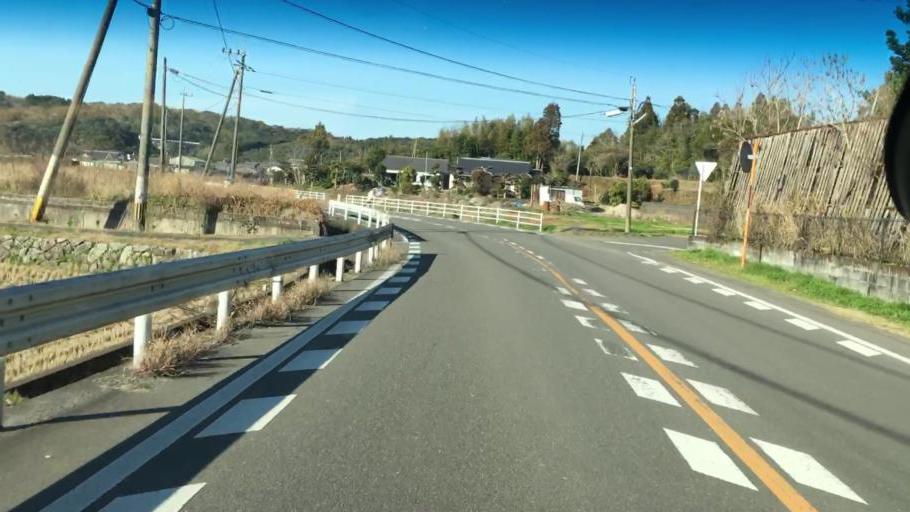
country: JP
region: Kagoshima
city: Satsumasendai
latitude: 31.8275
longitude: 130.2471
